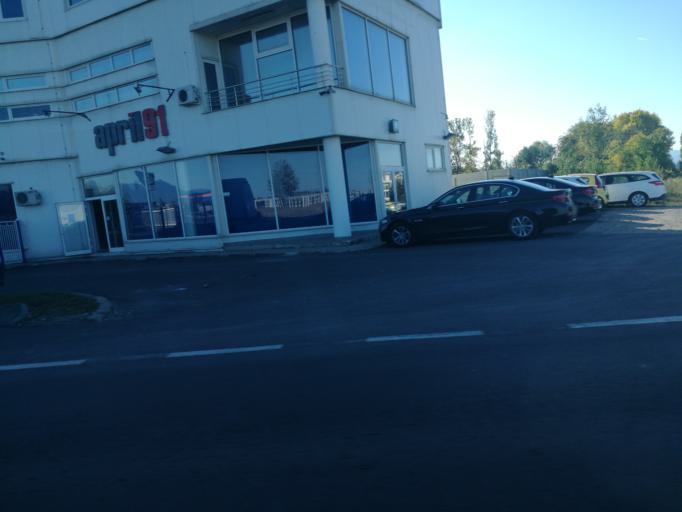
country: RO
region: Brasov
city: Brasov
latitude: 45.6806
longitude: 25.5857
